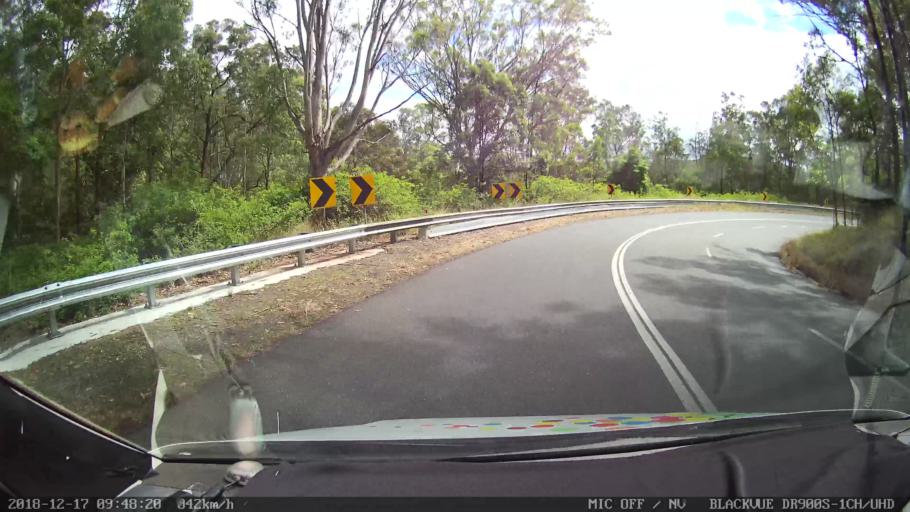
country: AU
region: New South Wales
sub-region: Tenterfield Municipality
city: Carrolls Creek
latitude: -28.9240
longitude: 152.3437
